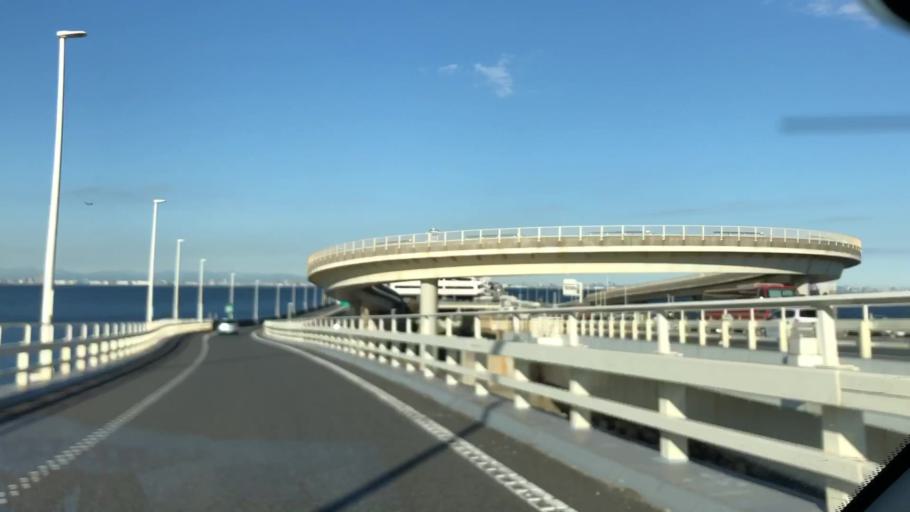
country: JP
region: Chiba
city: Kisarazu
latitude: 35.4609
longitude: 139.8791
